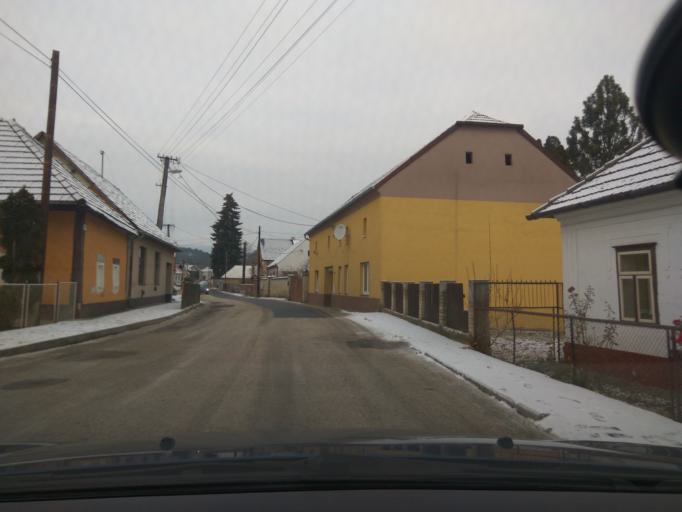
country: SK
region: Nitriansky
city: Stara Tura
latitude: 48.7805
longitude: 17.7378
